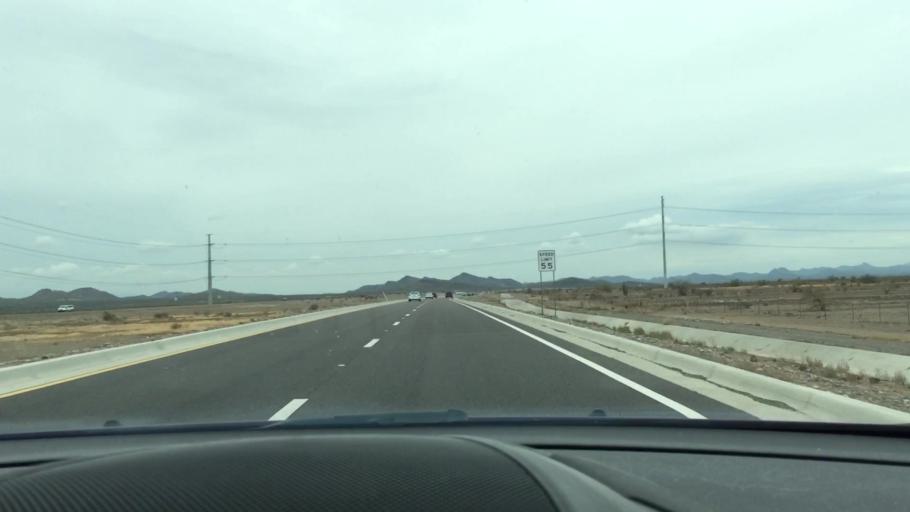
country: US
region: Arizona
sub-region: Maricopa County
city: Anthem
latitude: 33.7698
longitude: -112.1377
